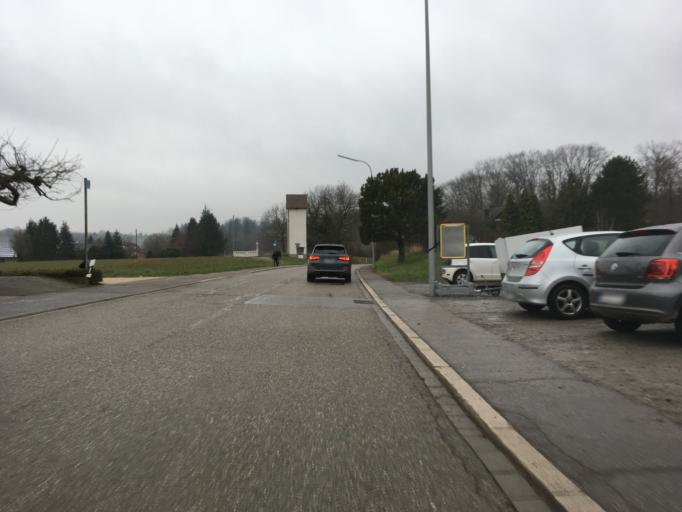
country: DE
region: Baden-Wuerttemberg
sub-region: Karlsruhe Region
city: Weingarten
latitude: 48.9680
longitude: 8.5042
